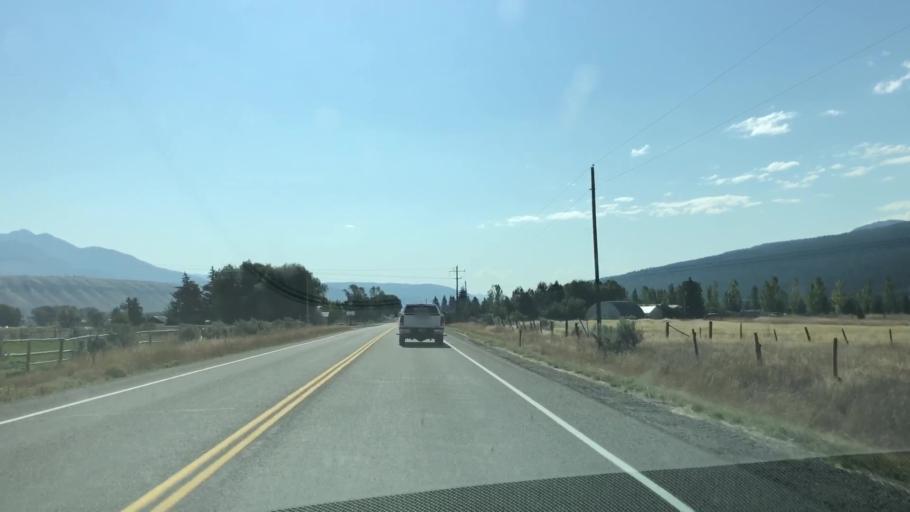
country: US
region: Idaho
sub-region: Teton County
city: Victor
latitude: 43.4033
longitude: -111.2912
